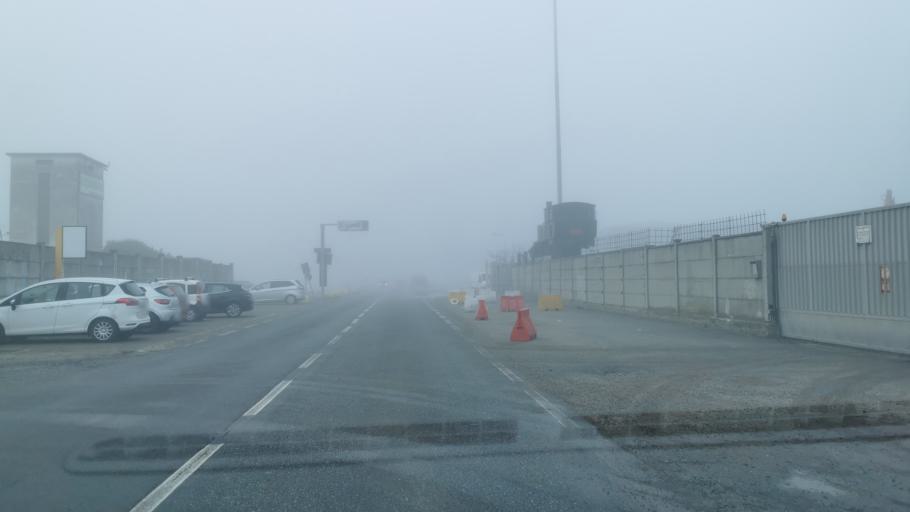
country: IT
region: Piedmont
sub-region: Provincia di Torino
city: Volpiano
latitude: 45.1916
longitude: 7.7524
